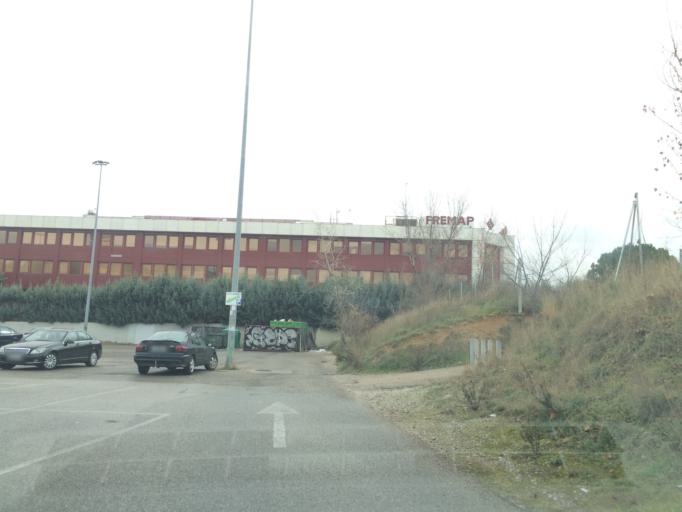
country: ES
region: Madrid
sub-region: Provincia de Madrid
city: Tres Cantos
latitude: 40.6053
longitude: -3.7181
